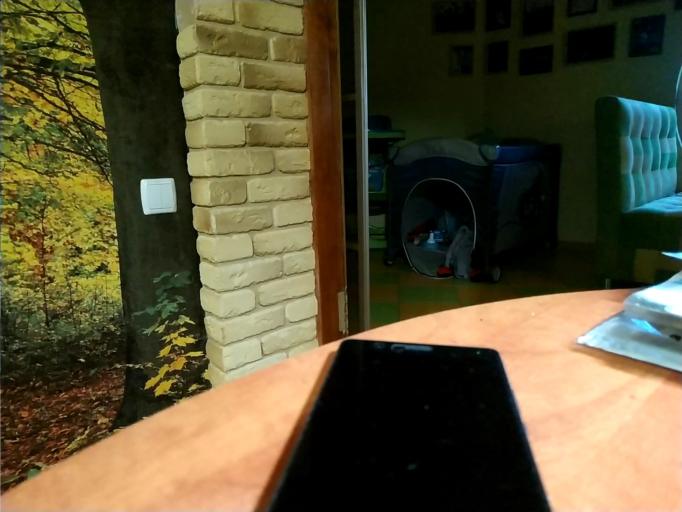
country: RU
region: Orjol
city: Znamenskoye
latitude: 53.4172
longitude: 35.5388
